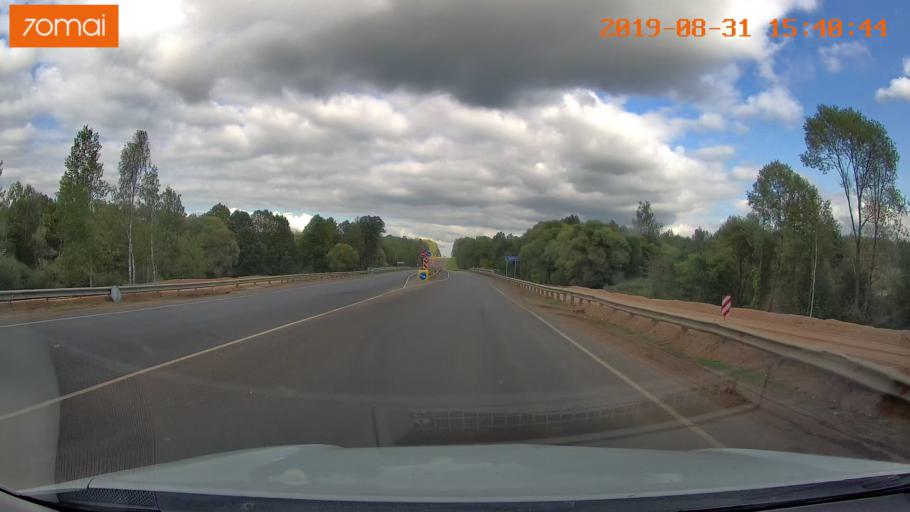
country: RU
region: Kaluga
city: Mosal'sk
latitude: 54.6345
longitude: 34.8438
